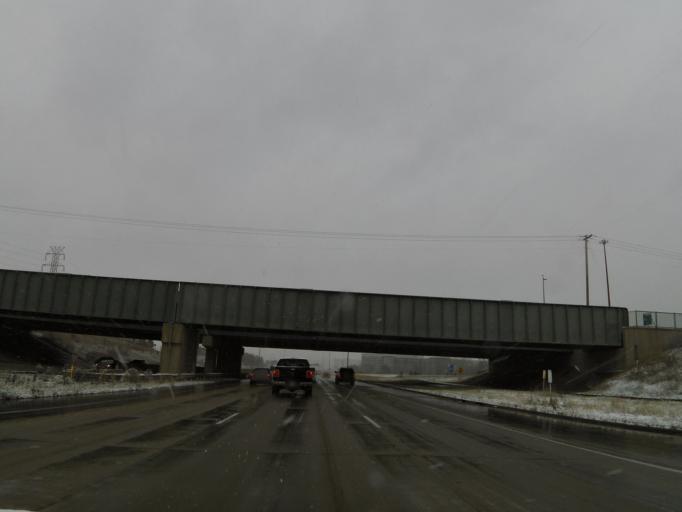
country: US
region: Minnesota
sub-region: Hennepin County
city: Edina
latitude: 44.8596
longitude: -93.3635
